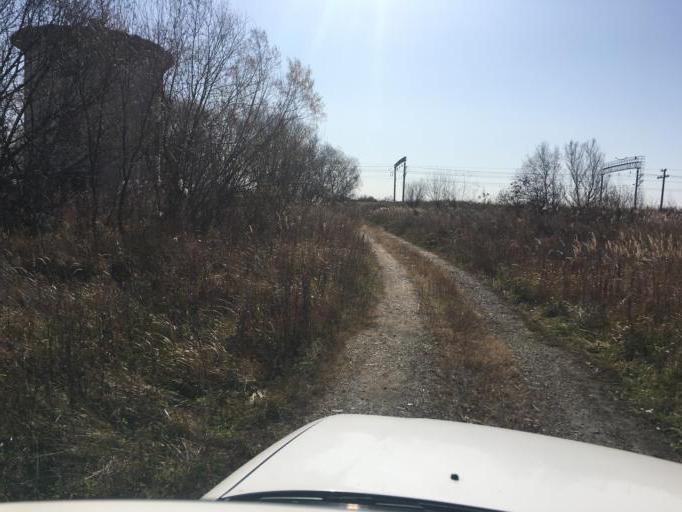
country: RU
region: Primorskiy
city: Dal'nerechensk
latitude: 45.9111
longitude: 133.7899
